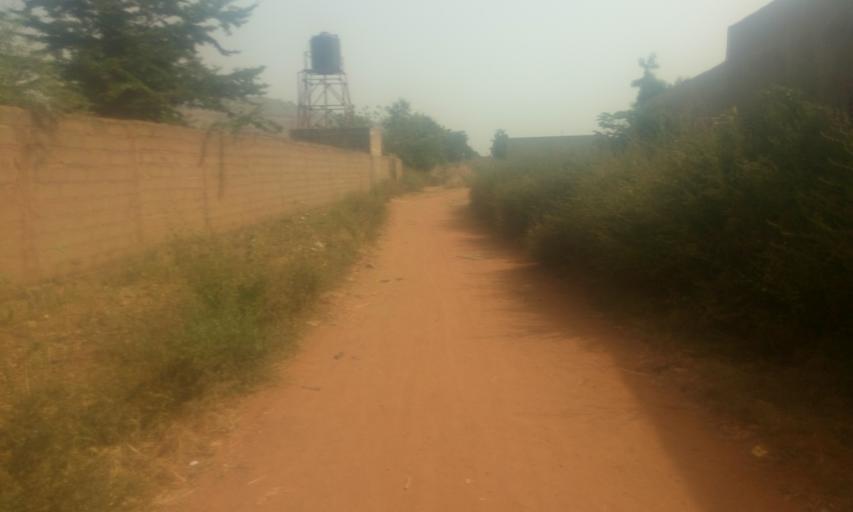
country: ML
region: Bamako
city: Bamako
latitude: 12.5834
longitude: -8.0779
